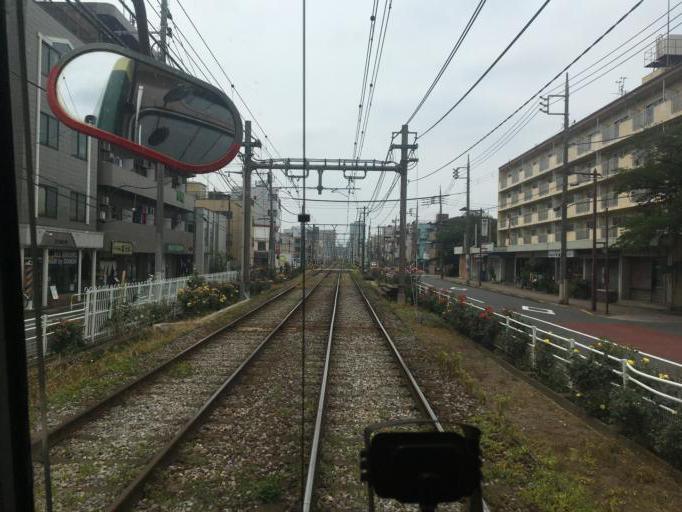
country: JP
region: Saitama
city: Kawaguchi
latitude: 35.7507
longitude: 139.7568
